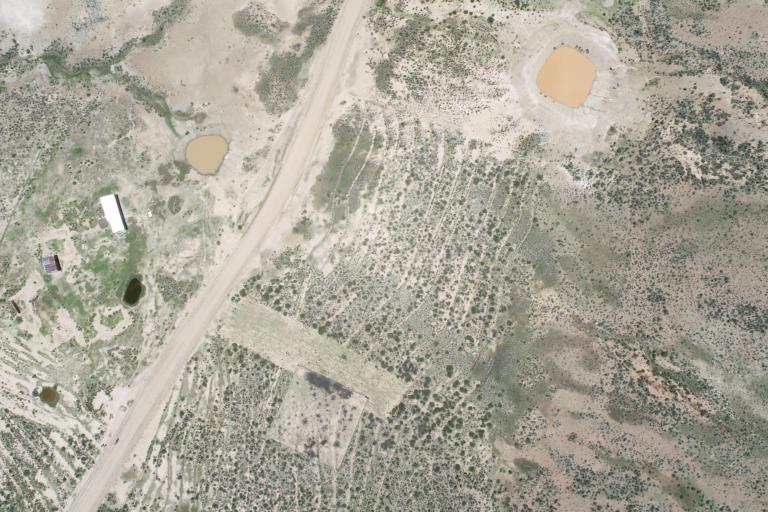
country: BO
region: La Paz
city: Curahuara de Carangas
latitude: -17.3081
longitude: -68.4944
